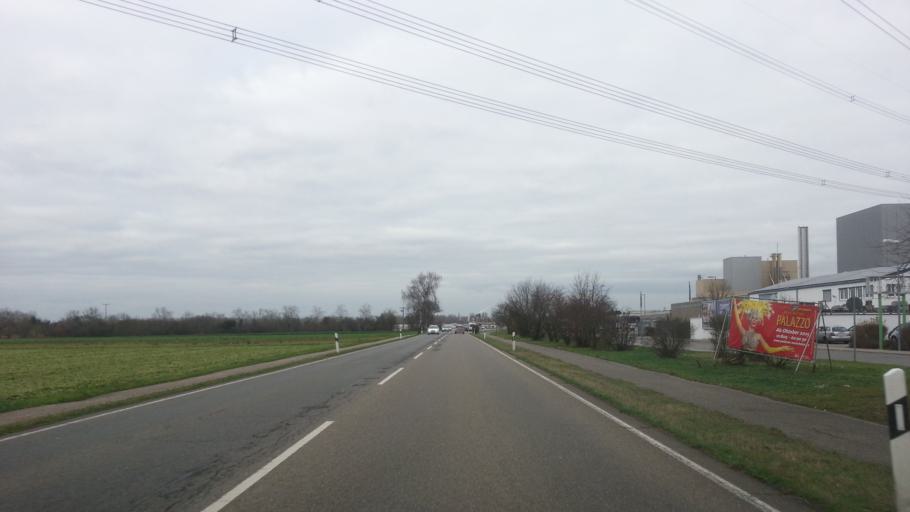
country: DE
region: Baden-Wuerttemberg
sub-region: Karlsruhe Region
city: Ketsch
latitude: 49.3507
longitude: 8.5289
